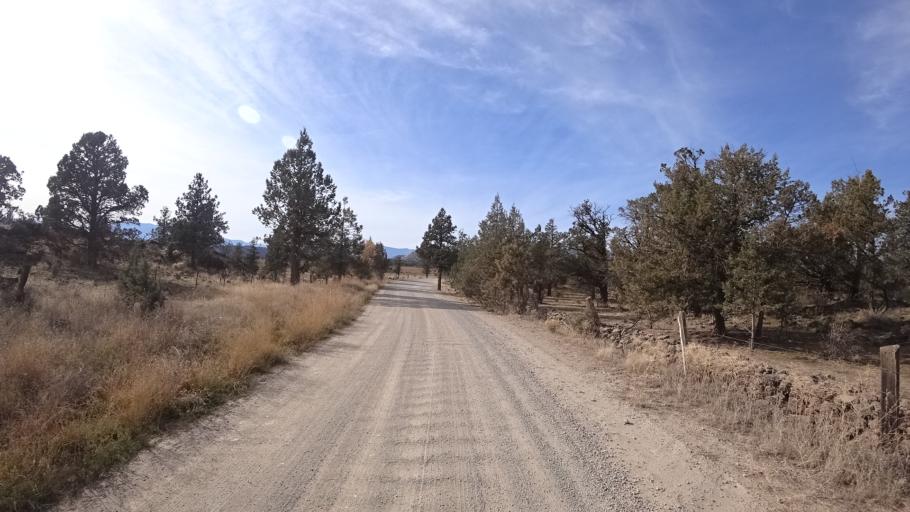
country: US
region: California
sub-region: Siskiyou County
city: Montague
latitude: 41.5955
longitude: -122.4173
